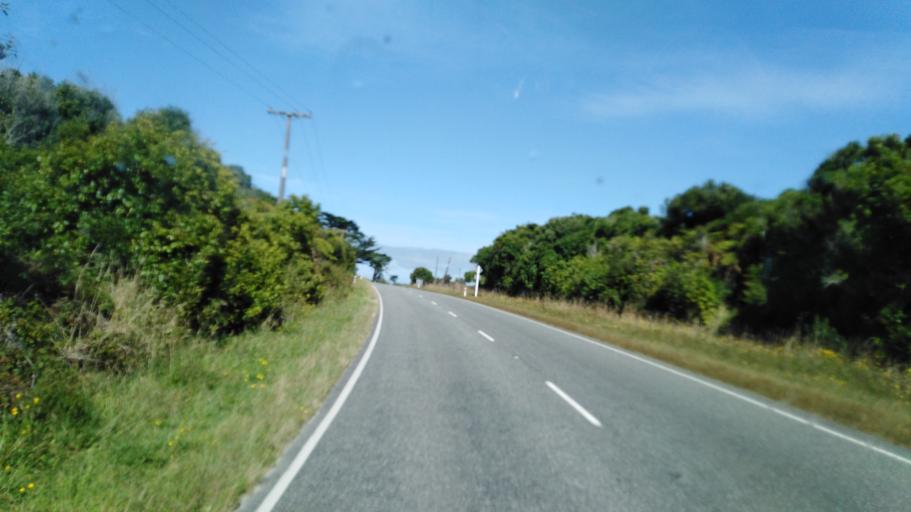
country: NZ
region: West Coast
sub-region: Buller District
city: Westport
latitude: -41.2906
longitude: 172.0968
